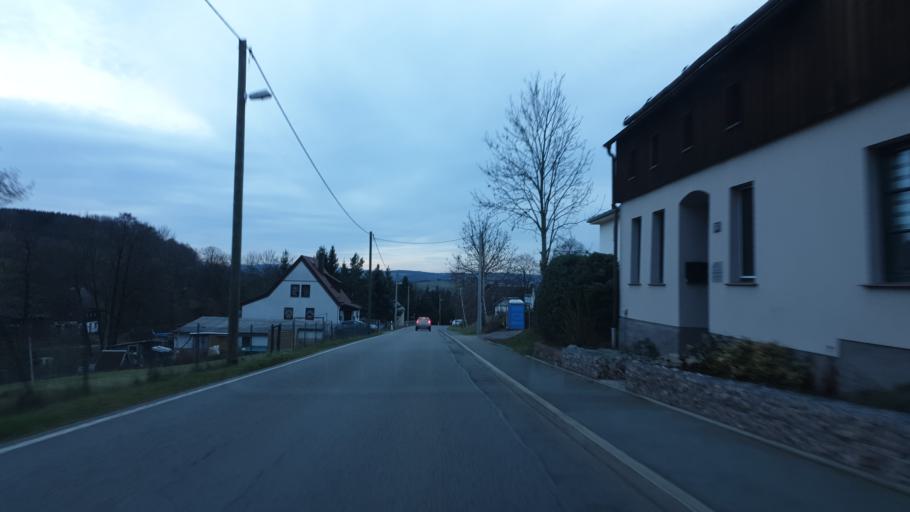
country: DE
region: Saxony
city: Hartenstein
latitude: 50.6940
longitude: 12.6751
